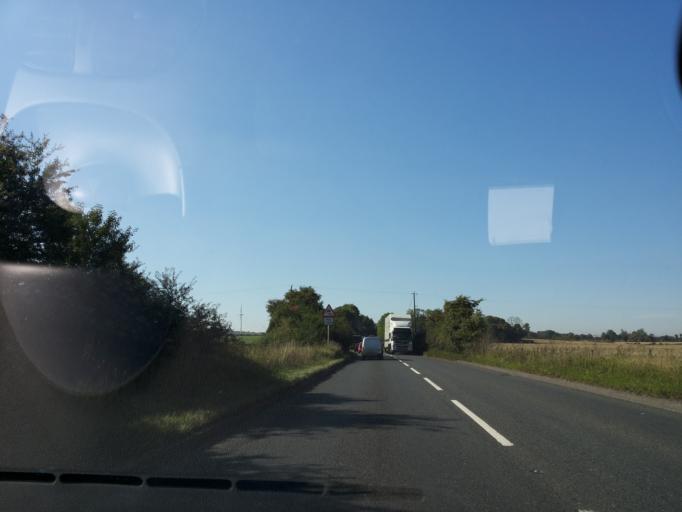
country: GB
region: England
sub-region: Doncaster
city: Marr
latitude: 53.5422
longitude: -1.2082
